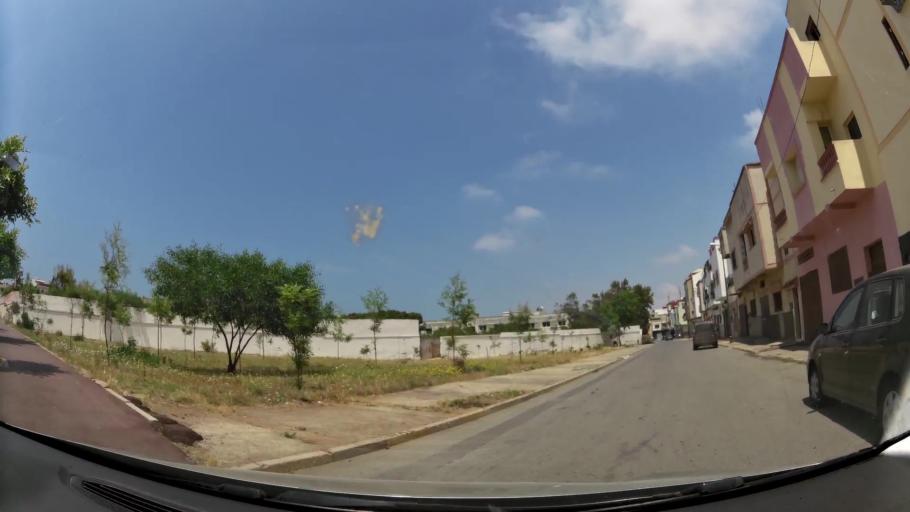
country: MA
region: Rabat-Sale-Zemmour-Zaer
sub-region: Skhirate-Temara
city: Temara
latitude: 33.9708
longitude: -6.8952
